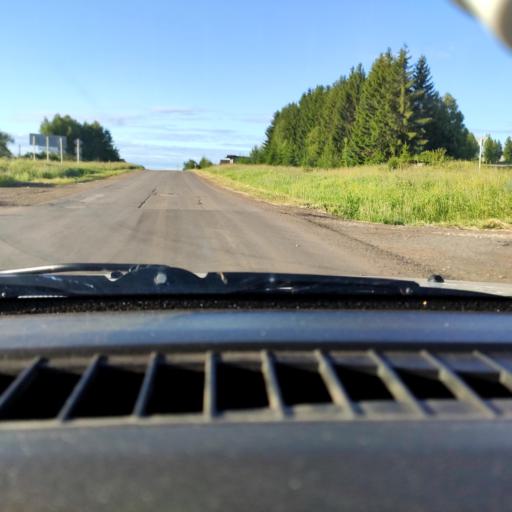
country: RU
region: Perm
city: Uinskoye
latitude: 57.1087
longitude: 56.5317
